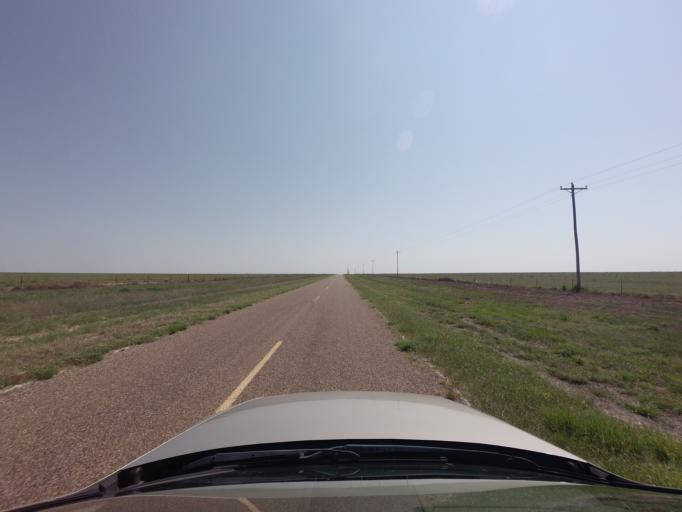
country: US
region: New Mexico
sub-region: Curry County
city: Cannon Air Force Base
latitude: 34.6331
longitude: -103.3775
